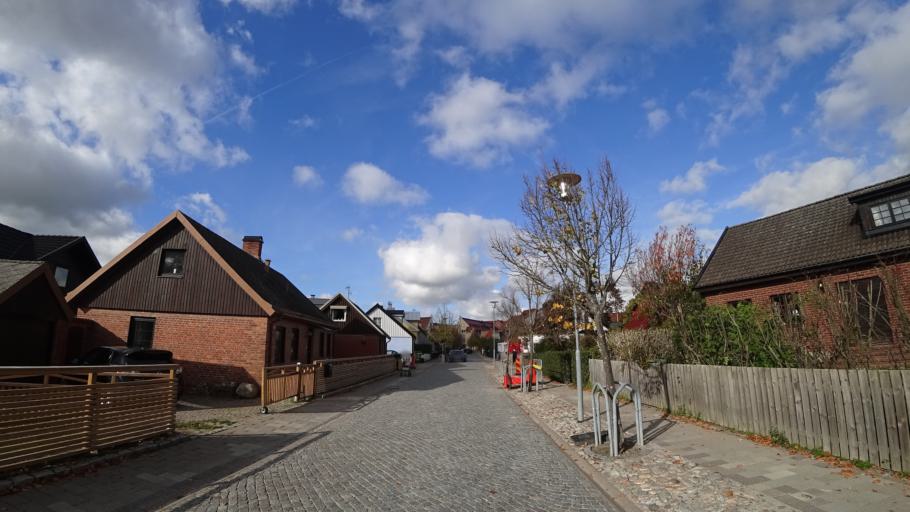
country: SE
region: Skane
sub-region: Staffanstorps Kommun
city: Staffanstorp
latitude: 55.6424
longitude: 13.2112
